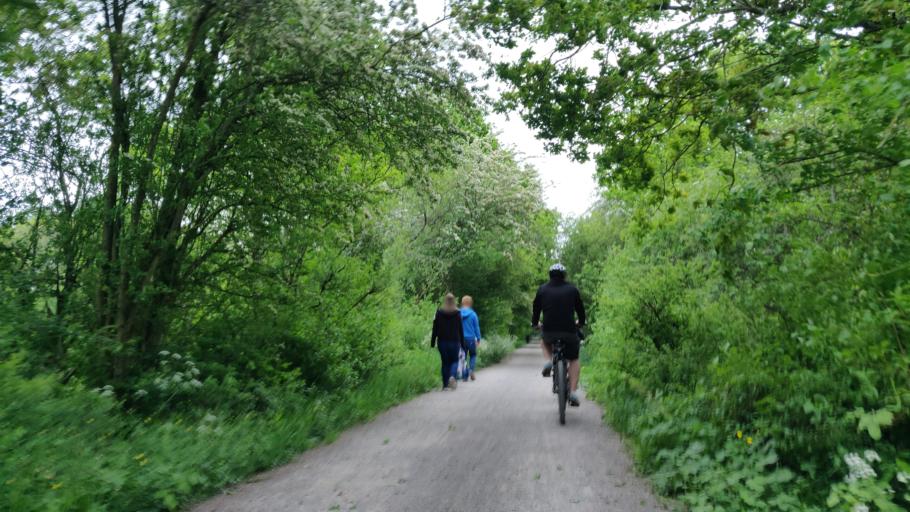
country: GB
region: England
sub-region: West Sussex
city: Southwater
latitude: 51.0091
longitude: -0.3301
